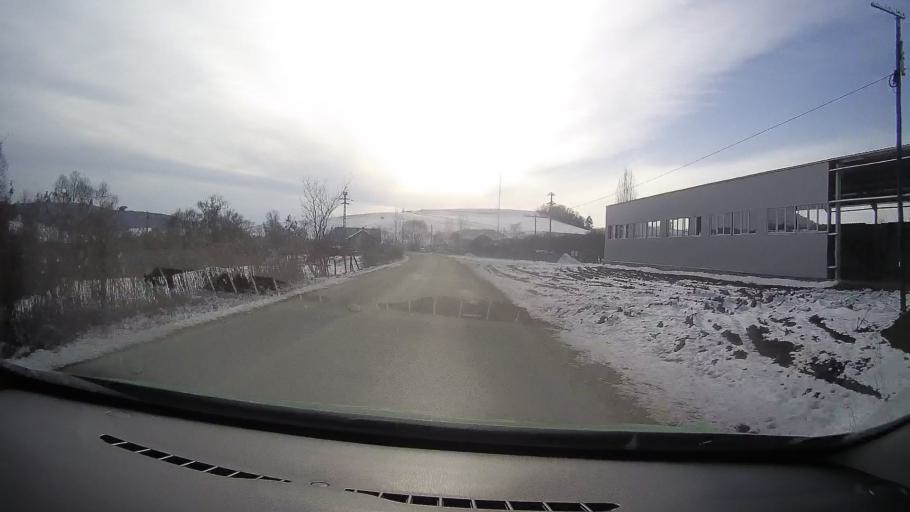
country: RO
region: Sibiu
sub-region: Oras Agnita
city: Ruja
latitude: 46.0032
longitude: 24.6742
